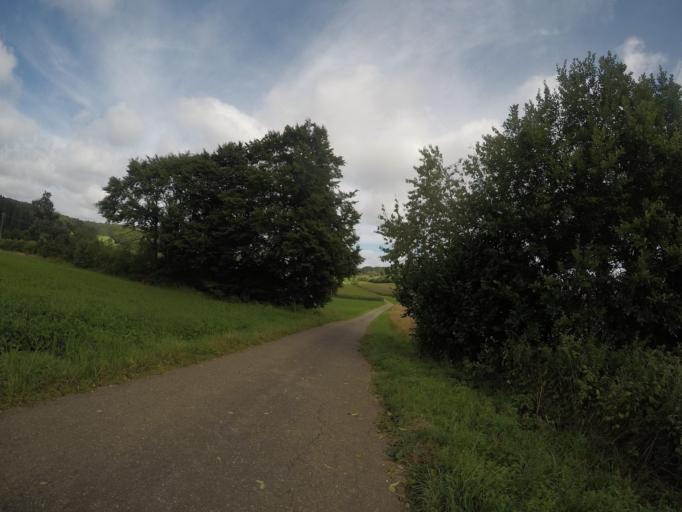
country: DE
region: Baden-Wuerttemberg
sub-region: Tuebingen Region
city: Westerheim
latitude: 48.4586
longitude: 9.6331
